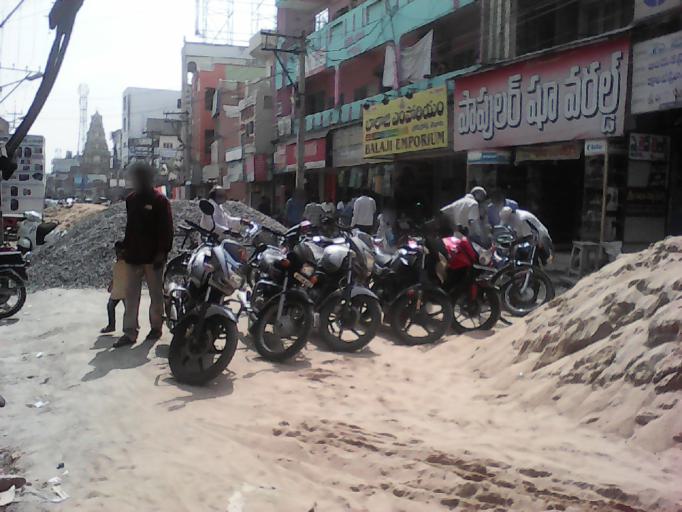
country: IN
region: Andhra Pradesh
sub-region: Guntur
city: Bhattiprolu
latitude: 16.2375
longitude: 80.6495
